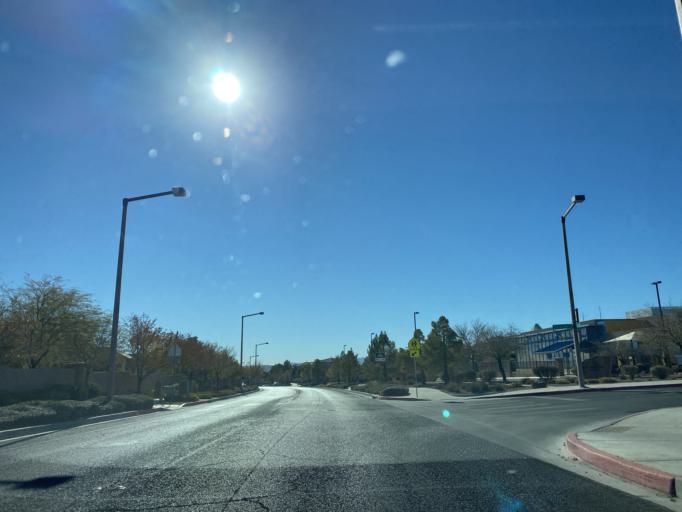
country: US
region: Nevada
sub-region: Clark County
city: Summerlin South
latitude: 36.1685
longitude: -115.3431
